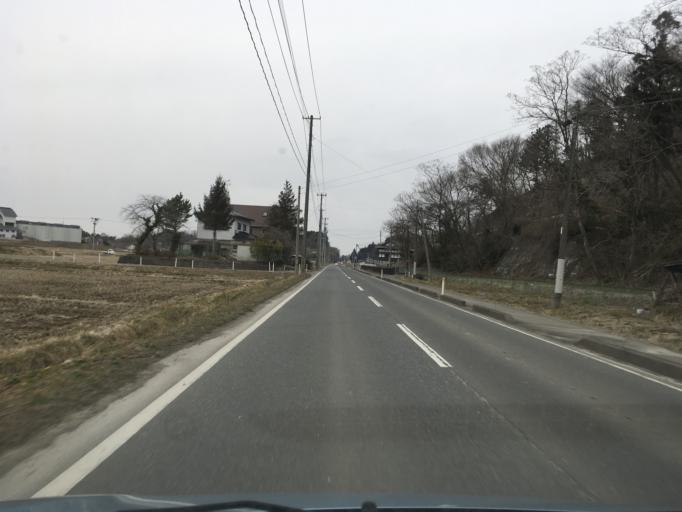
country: JP
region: Miyagi
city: Wakuya
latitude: 38.6603
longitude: 141.2764
